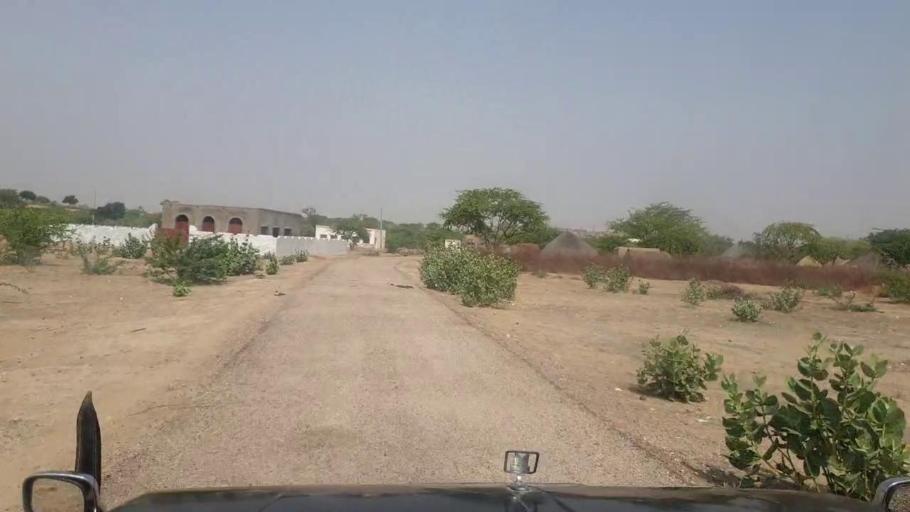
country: PK
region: Sindh
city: Islamkot
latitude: 25.0775
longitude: 70.1509
